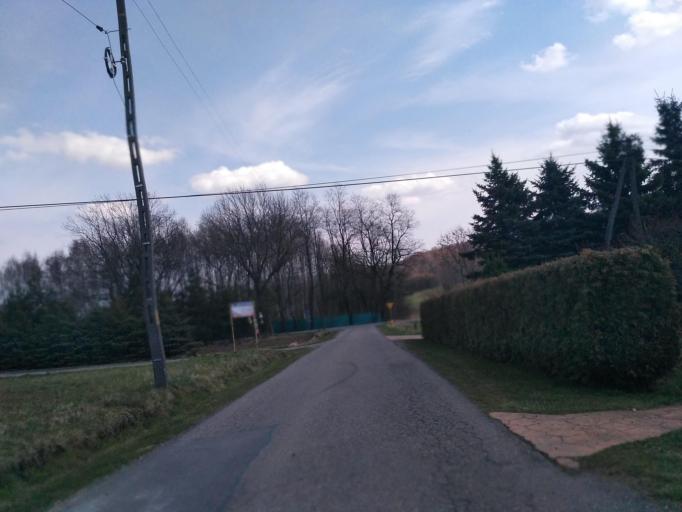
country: PL
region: Subcarpathian Voivodeship
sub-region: Powiat ropczycko-sedziszowski
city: Iwierzyce
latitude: 50.0463
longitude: 21.7439
